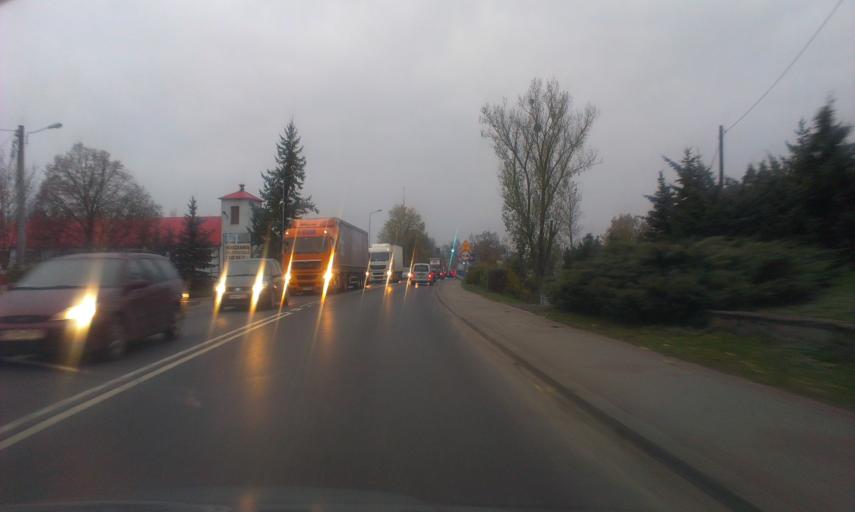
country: PL
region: Greater Poland Voivodeship
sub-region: Powiat pilski
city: Ujscie
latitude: 53.0539
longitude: 16.7314
